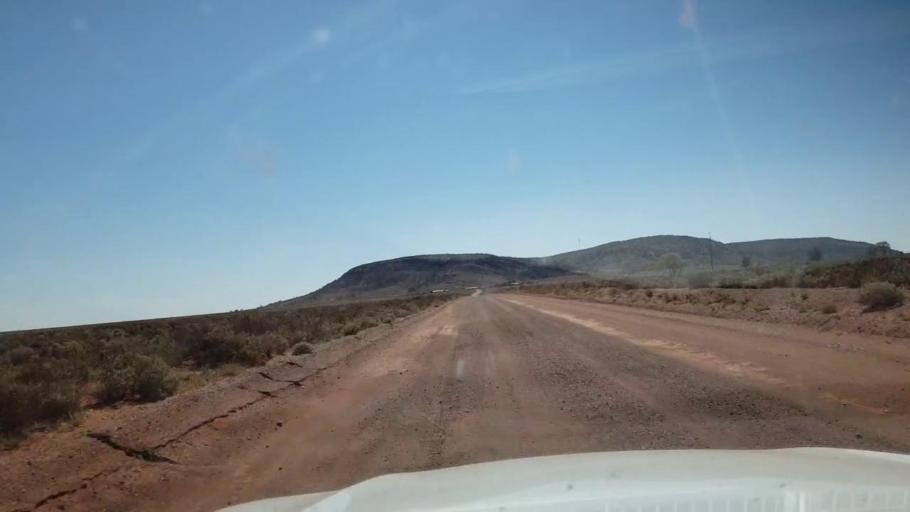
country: AU
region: South Australia
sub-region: Whyalla
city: Whyalla
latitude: -32.6988
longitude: 137.1332
